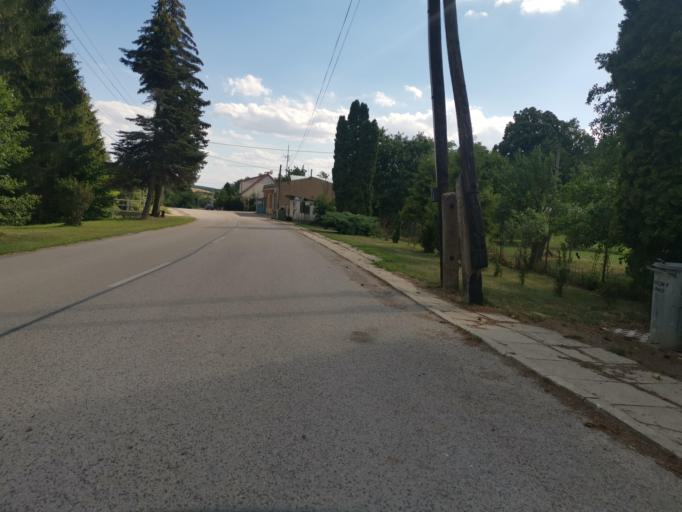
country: CZ
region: South Moravian
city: Knezdub
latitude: 48.7994
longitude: 17.4104
